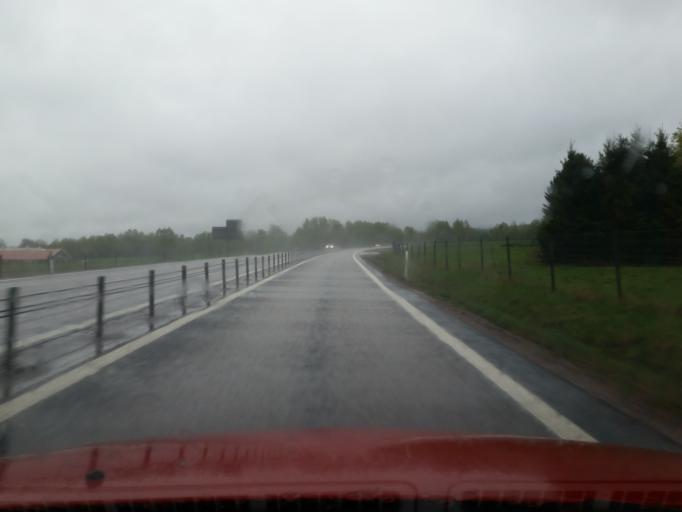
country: SE
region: Dalarna
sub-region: Borlange Kommun
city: Ornas
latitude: 60.4073
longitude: 15.6046
